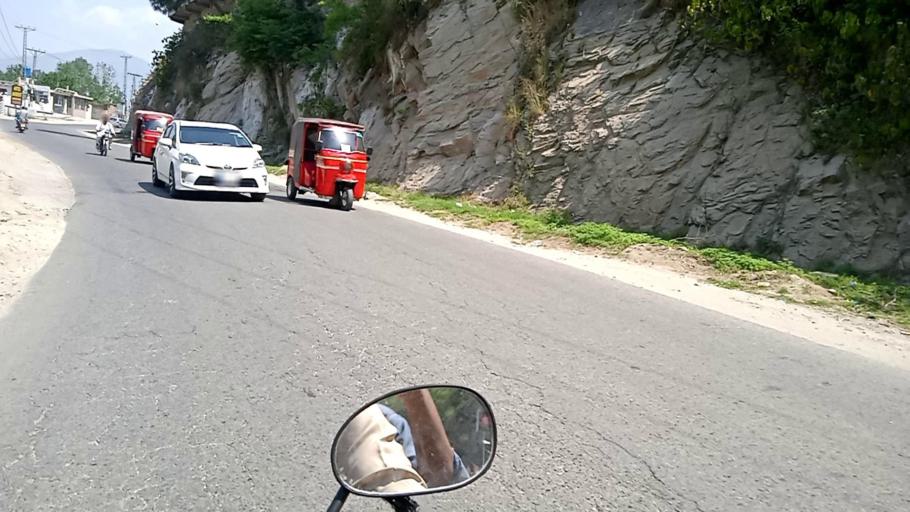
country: PK
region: Khyber Pakhtunkhwa
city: Mingora
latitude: 34.7923
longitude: 72.3939
